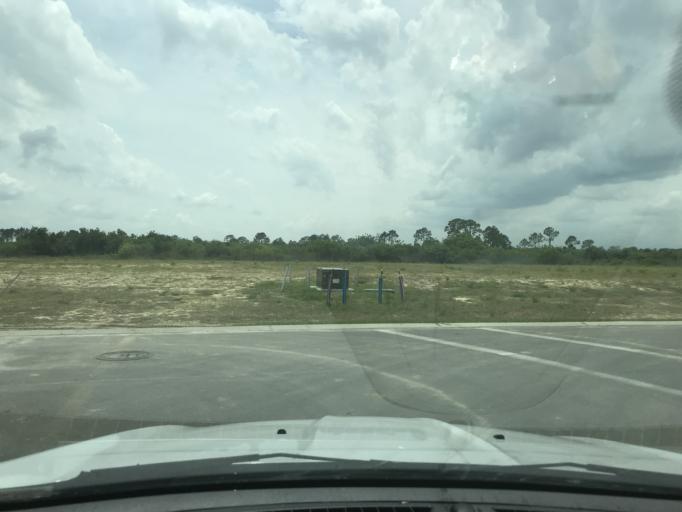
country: US
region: Florida
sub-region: Lee County
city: Olga
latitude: 26.7770
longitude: -81.7433
